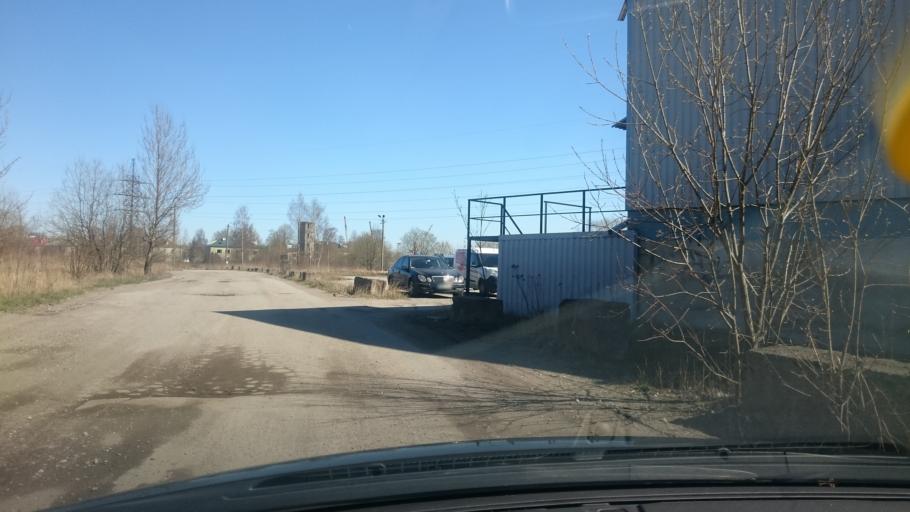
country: EE
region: Harju
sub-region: Tallinna linn
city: Tallinn
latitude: 59.4582
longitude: 24.6928
